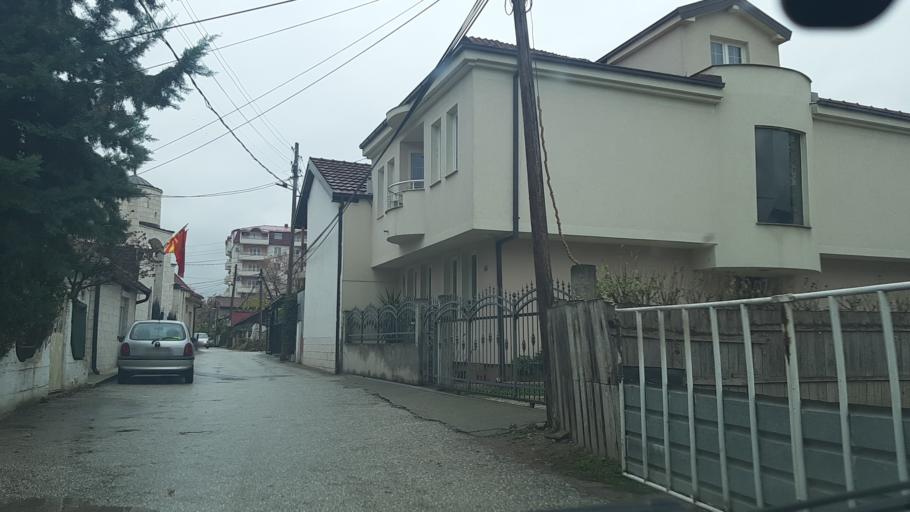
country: MK
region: Karpos
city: Skopje
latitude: 41.9944
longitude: 21.4467
